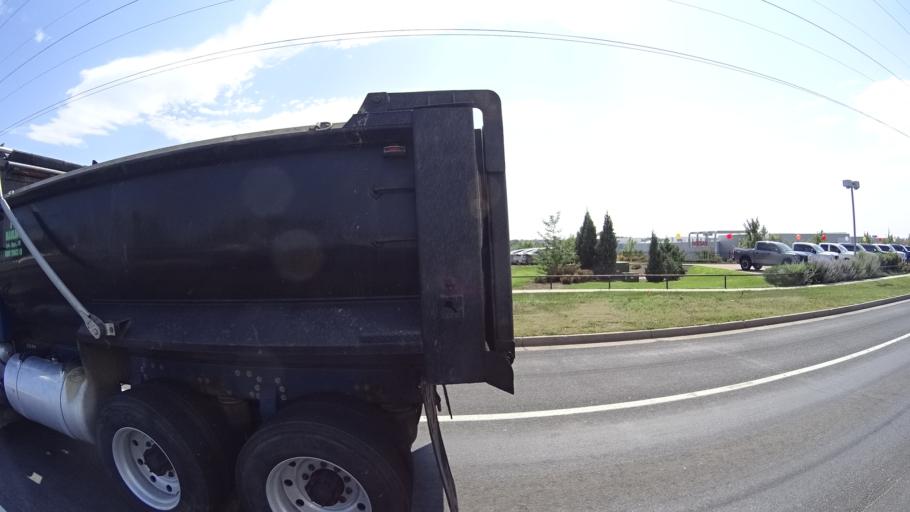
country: US
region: Colorado
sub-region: El Paso County
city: Stratmoor
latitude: 38.8131
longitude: -104.7574
